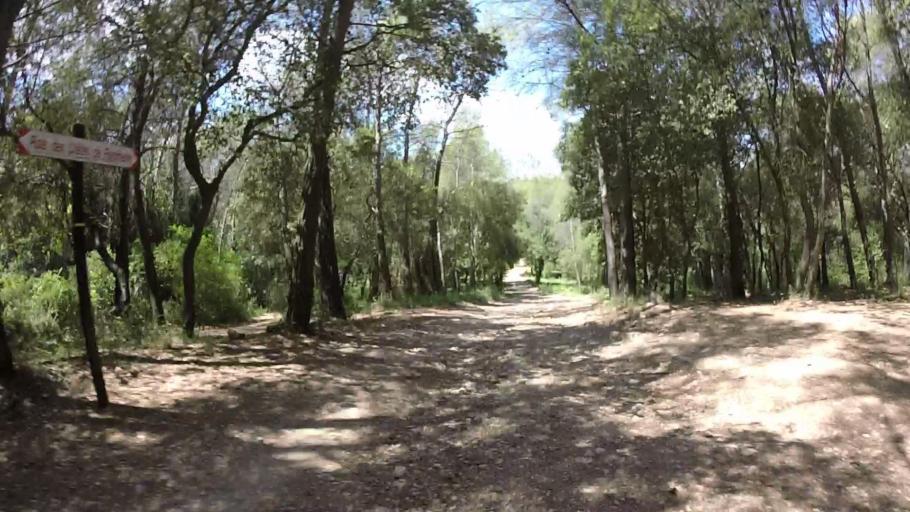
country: FR
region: Provence-Alpes-Cote d'Azur
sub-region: Departement des Alpes-Maritimes
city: Le Cannet
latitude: 43.5964
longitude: 7.0305
